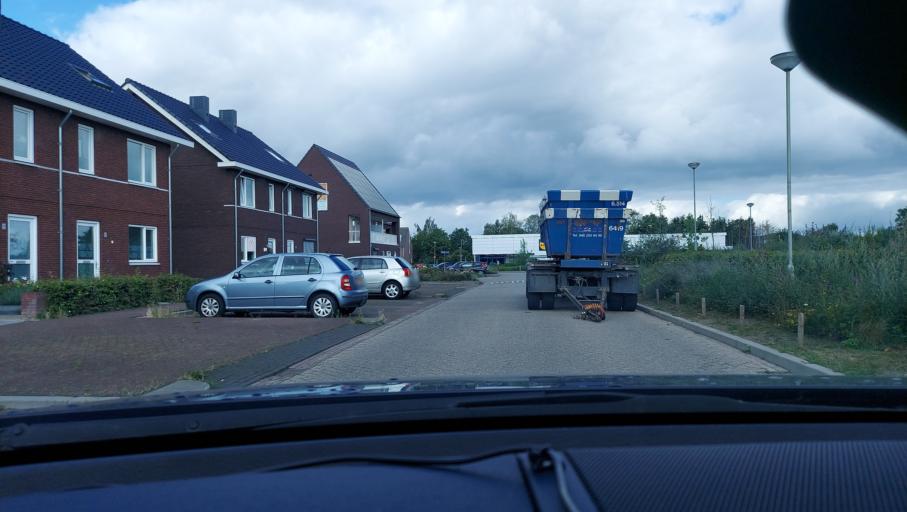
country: NL
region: Limburg
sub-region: Gemeente Beesel
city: Reuver
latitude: 51.2839
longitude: 6.0838
